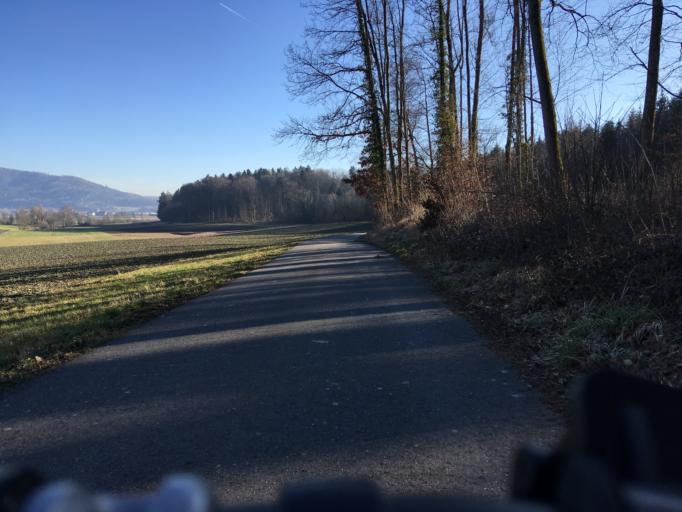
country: CH
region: Schaffhausen
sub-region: Bezirk Stein
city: Ramsen
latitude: 47.7254
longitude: 8.8024
